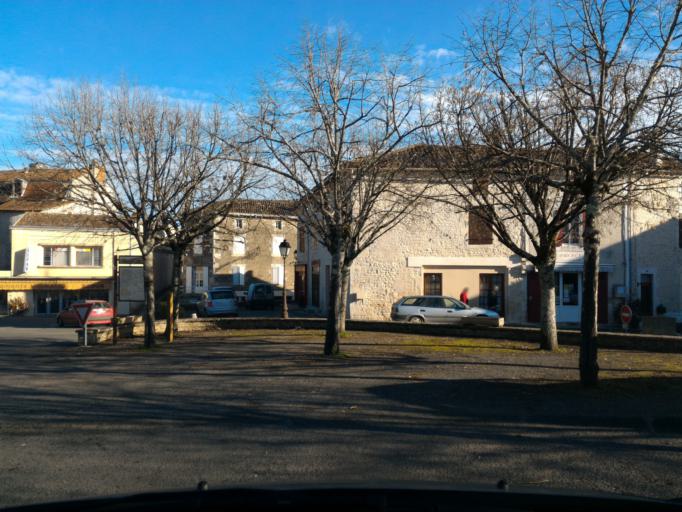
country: FR
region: Poitou-Charentes
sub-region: Departement de la Charente
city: Champagne-Mouton
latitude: 45.9918
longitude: 0.4116
